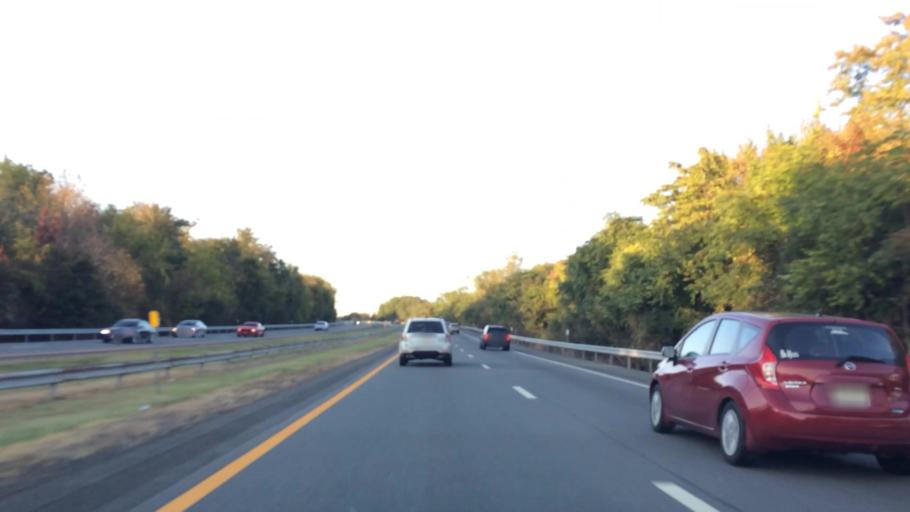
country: US
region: New York
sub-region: Orange County
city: Vails Gate
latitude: 41.4486
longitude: -74.0651
